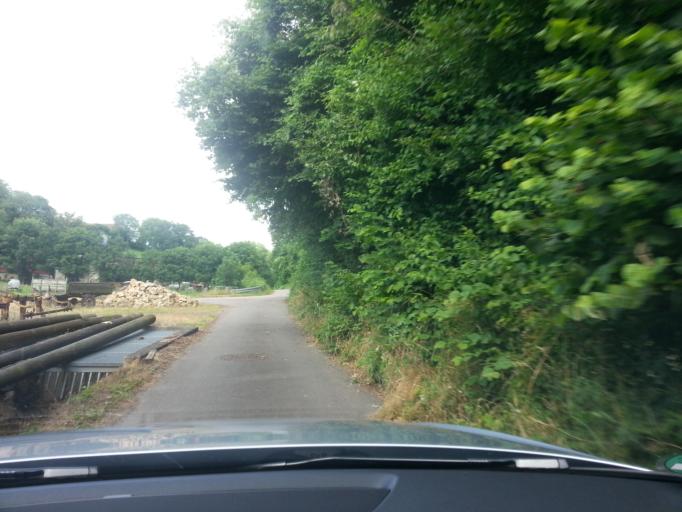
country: DE
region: Rheinland-Pfalz
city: Kirf
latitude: 49.5321
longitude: 6.4266
